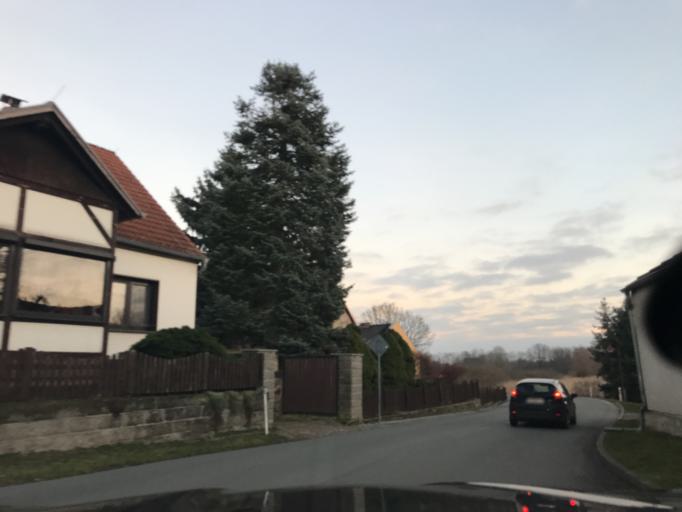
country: DE
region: Brandenburg
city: Pawesin
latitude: 52.5141
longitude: 12.7023
